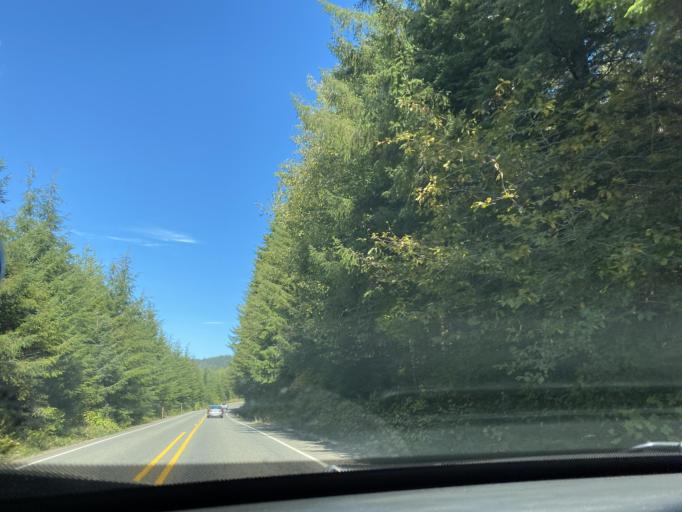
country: US
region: Washington
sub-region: Clallam County
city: Forks
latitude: 47.9485
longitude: -124.4623
